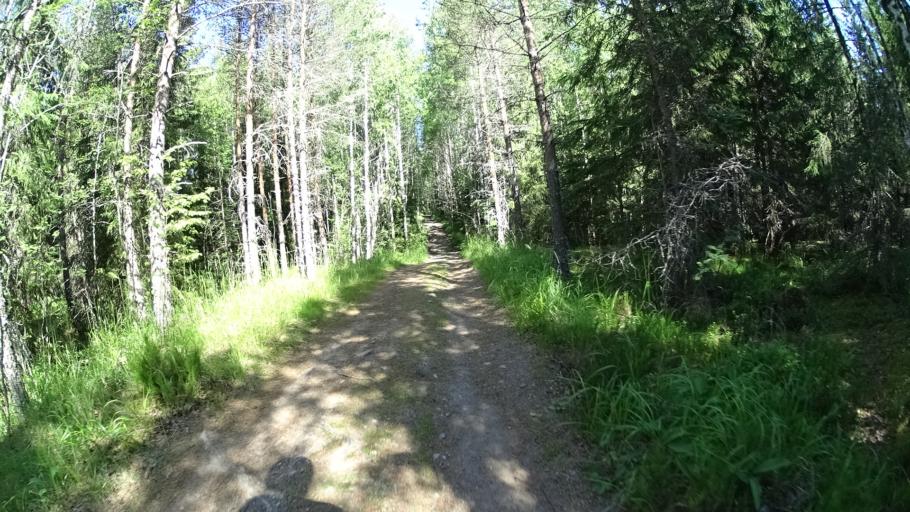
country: FI
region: Uusimaa
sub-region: Helsinki
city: Espoo
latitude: 60.3160
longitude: 24.5028
